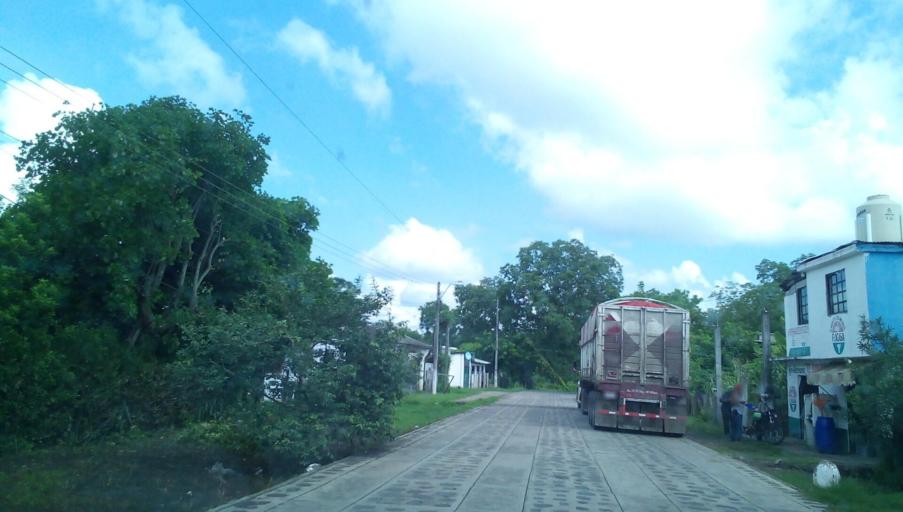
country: MX
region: Veracruz
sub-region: Citlaltepetl
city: Las Sabinas
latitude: 21.3631
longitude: -97.9017
